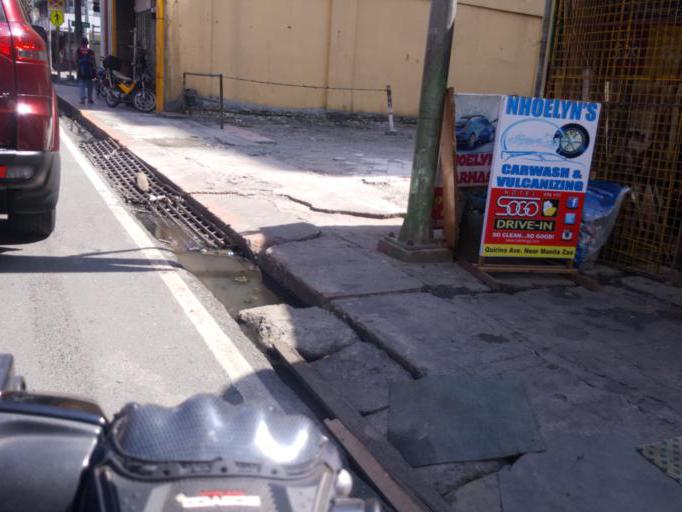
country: PH
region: Metro Manila
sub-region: City of Manila
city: Port Area
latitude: 14.5800
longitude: 120.9790
